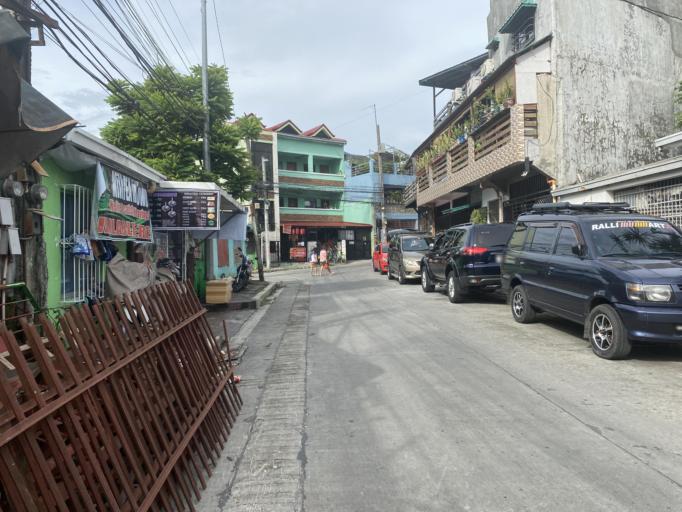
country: PH
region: Calabarzon
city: Bagong Pagasa
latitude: 14.7047
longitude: 121.0524
